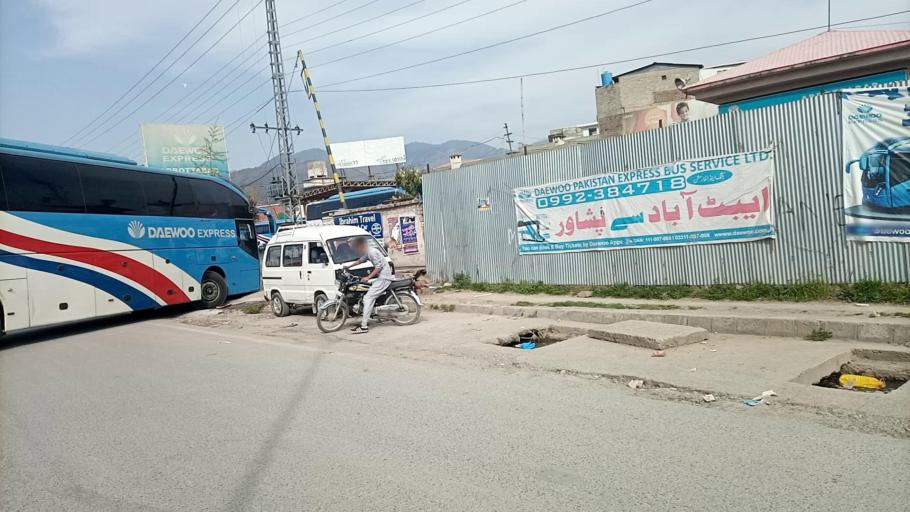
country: PK
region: Khyber Pakhtunkhwa
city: Abbottabad
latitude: 34.1924
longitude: 73.2349
